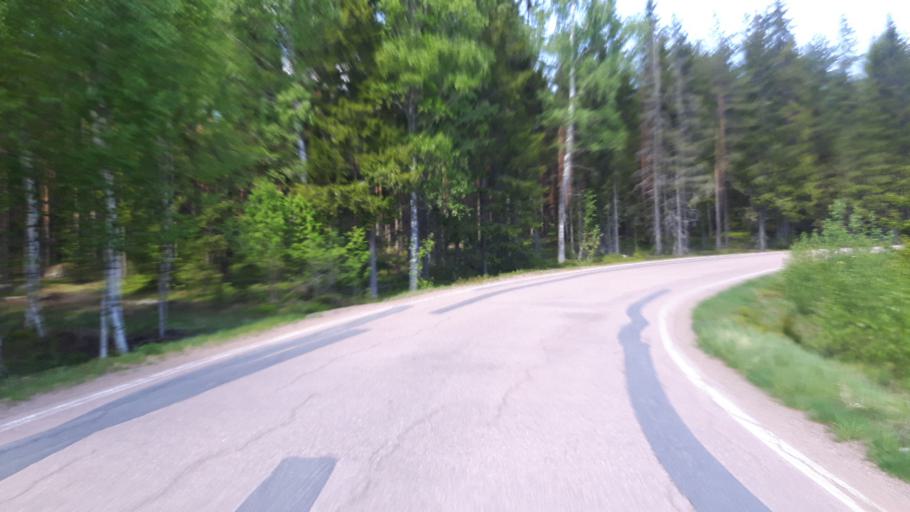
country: FI
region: Kymenlaakso
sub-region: Kotka-Hamina
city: Virolahti
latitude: 60.5391
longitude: 27.6177
